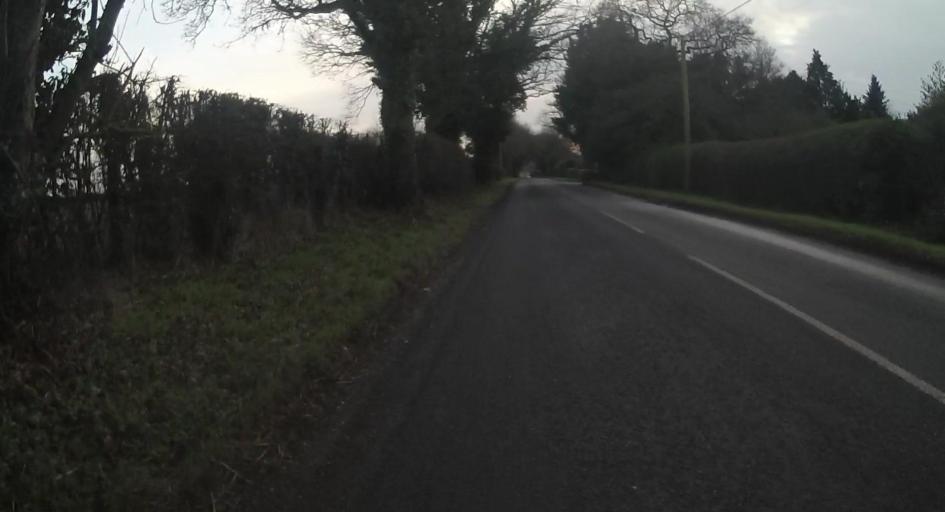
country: GB
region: England
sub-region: Hampshire
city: Overton
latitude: 51.2497
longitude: -1.3320
